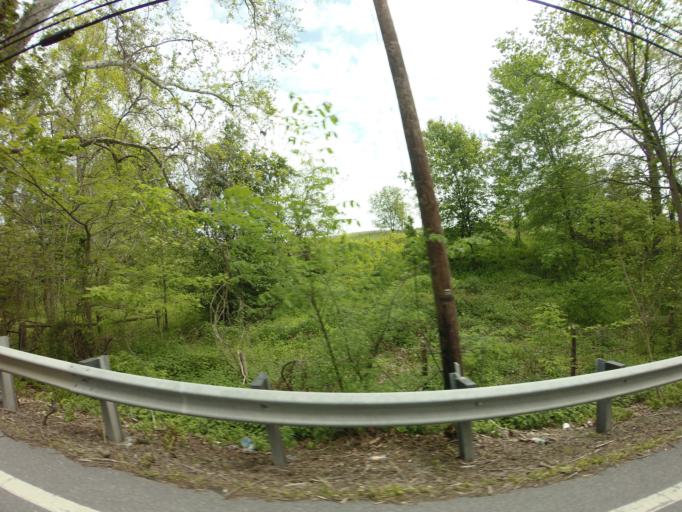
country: US
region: Maryland
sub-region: Frederick County
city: Urbana
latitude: 39.3202
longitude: -77.3374
